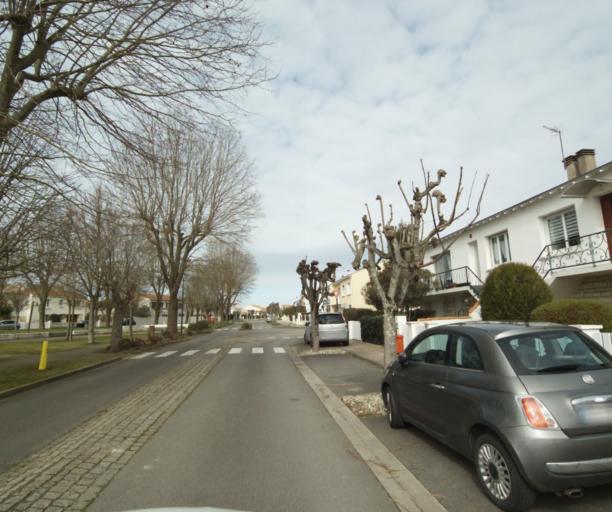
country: FR
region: Poitou-Charentes
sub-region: Departement de la Charente-Maritime
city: Lagord
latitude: 46.1851
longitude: -1.1569
